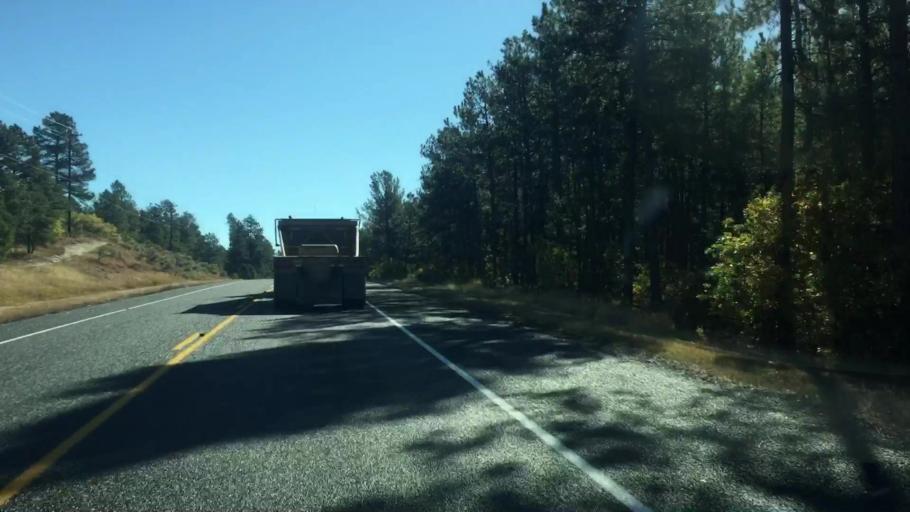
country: US
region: Colorado
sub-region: Elbert County
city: Ponderosa Park
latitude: 39.3785
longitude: -104.7050
